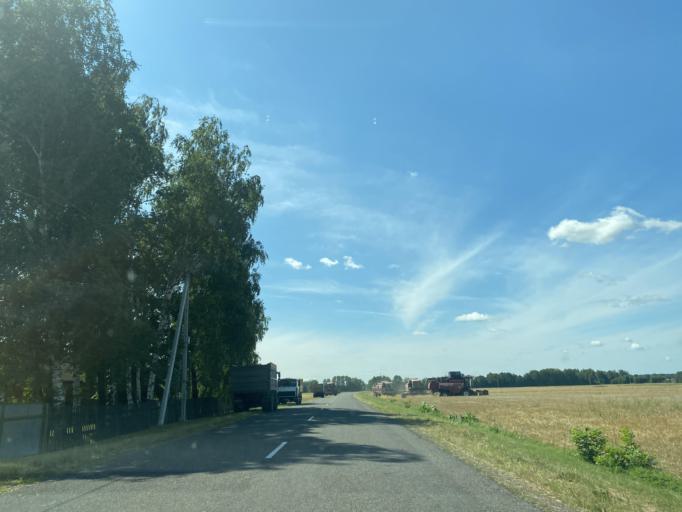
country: BY
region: Brest
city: Ivanava
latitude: 52.1972
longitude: 25.6131
